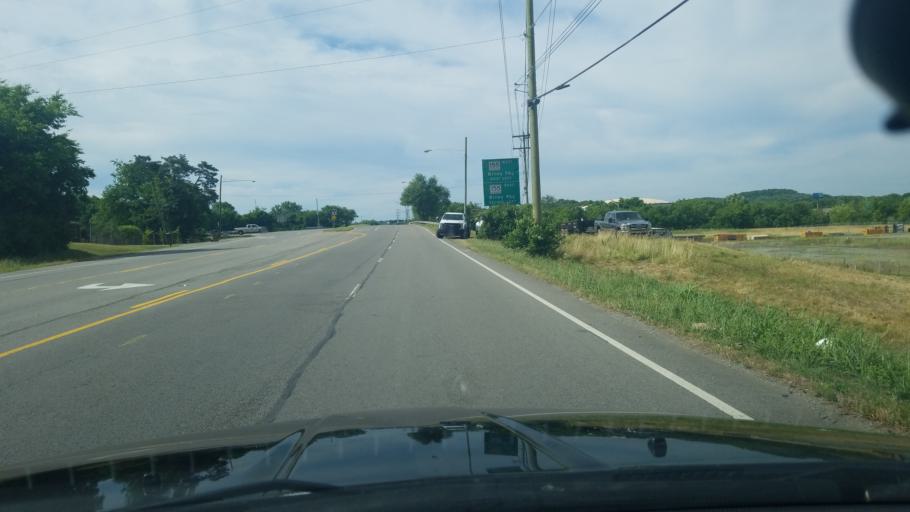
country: US
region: Tennessee
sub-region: Davidson County
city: Nashville
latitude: 36.2407
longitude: -86.7808
